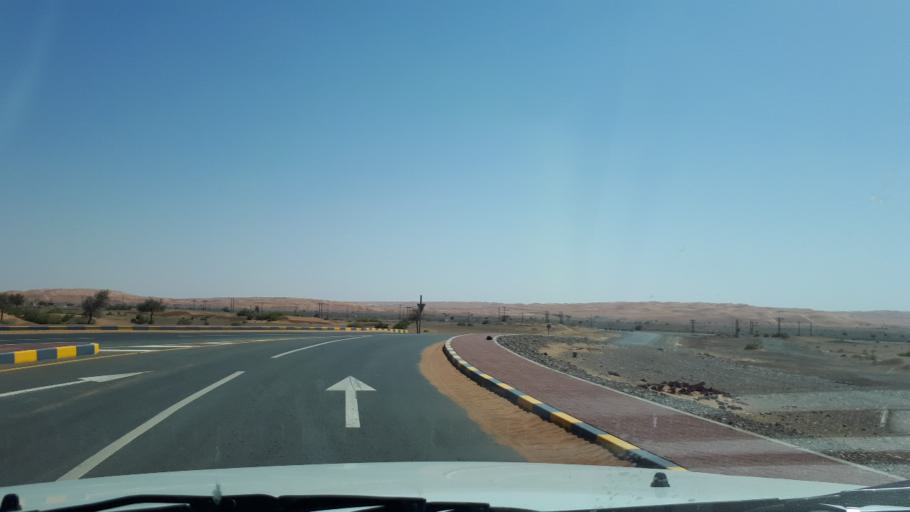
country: OM
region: Ash Sharqiyah
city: Al Qabil
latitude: 22.5224
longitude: 58.7401
